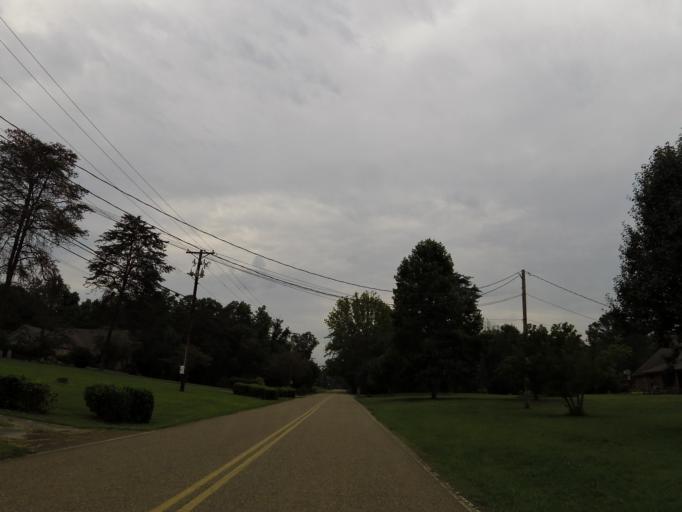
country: US
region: Tennessee
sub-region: Sevier County
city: Seymour
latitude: 35.9250
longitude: -83.8085
